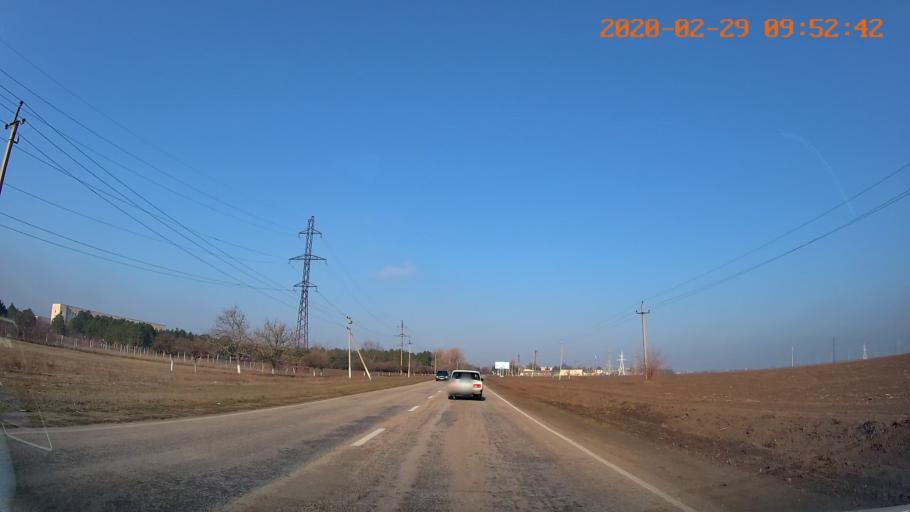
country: MD
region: Telenesti
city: Slobozia
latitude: 46.7174
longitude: 29.7282
